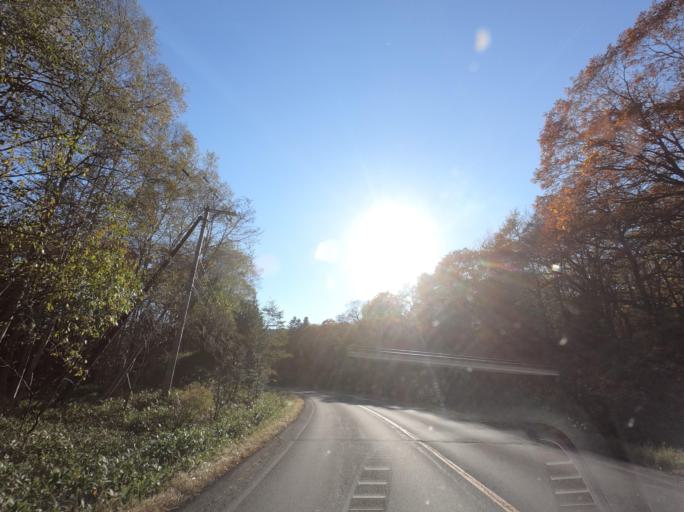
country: JP
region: Hokkaido
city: Bihoro
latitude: 43.3901
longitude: 144.1327
